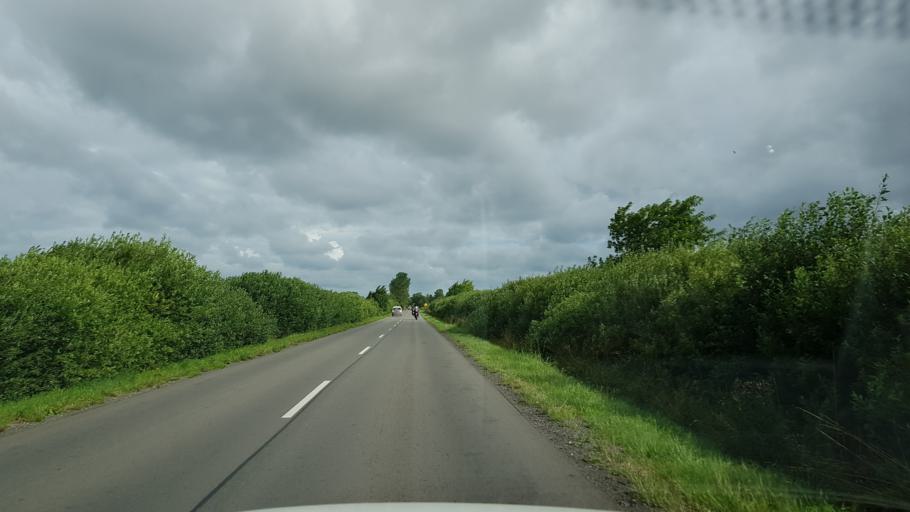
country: PL
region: West Pomeranian Voivodeship
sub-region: Powiat gryficki
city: Karnice
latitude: 54.0487
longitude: 15.0302
